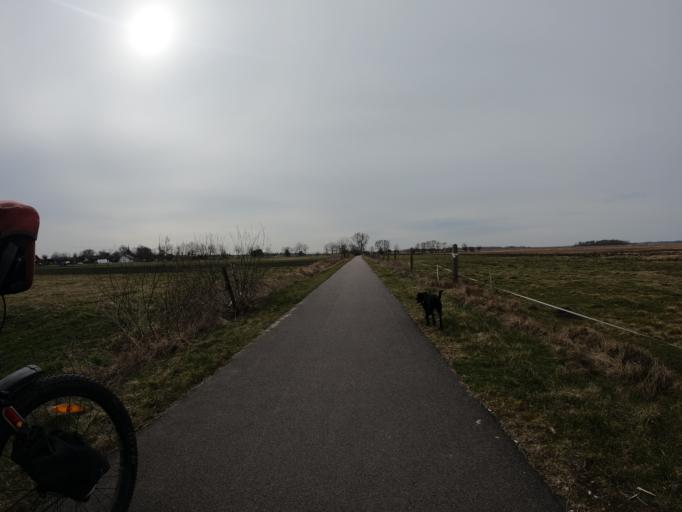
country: PL
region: West Pomeranian Voivodeship
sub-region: Powiat gryficki
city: Mrzezyno
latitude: 54.1257
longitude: 15.3145
